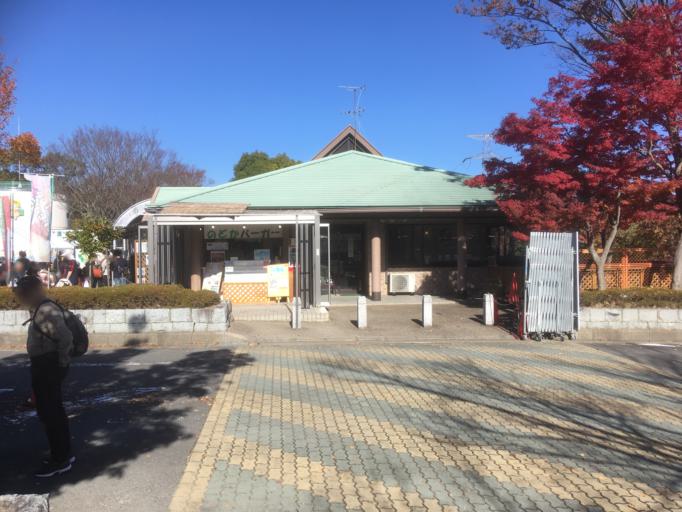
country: JP
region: Osaka
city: Kashihara
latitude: 34.6029
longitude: 135.6586
